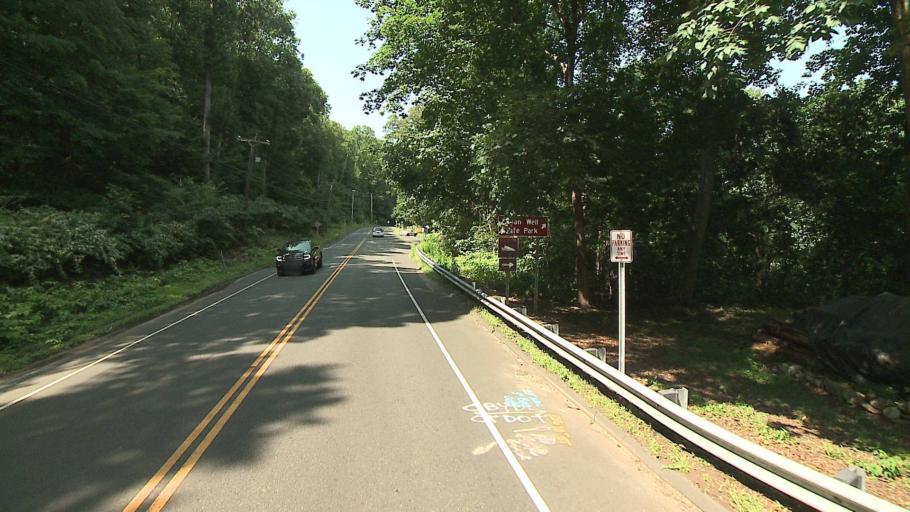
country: US
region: Connecticut
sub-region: Fairfield County
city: Shelton
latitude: 41.3327
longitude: -73.1202
